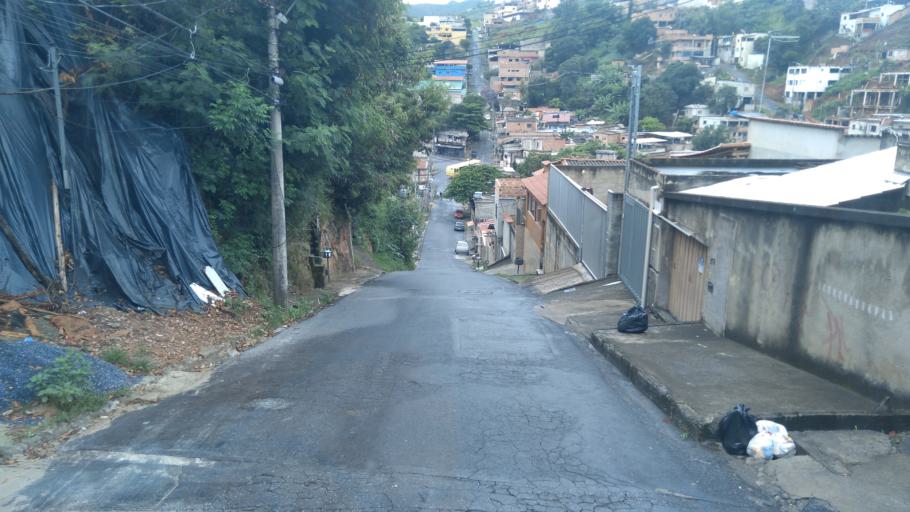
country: BR
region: Minas Gerais
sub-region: Belo Horizonte
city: Belo Horizonte
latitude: -19.9175
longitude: -43.8850
